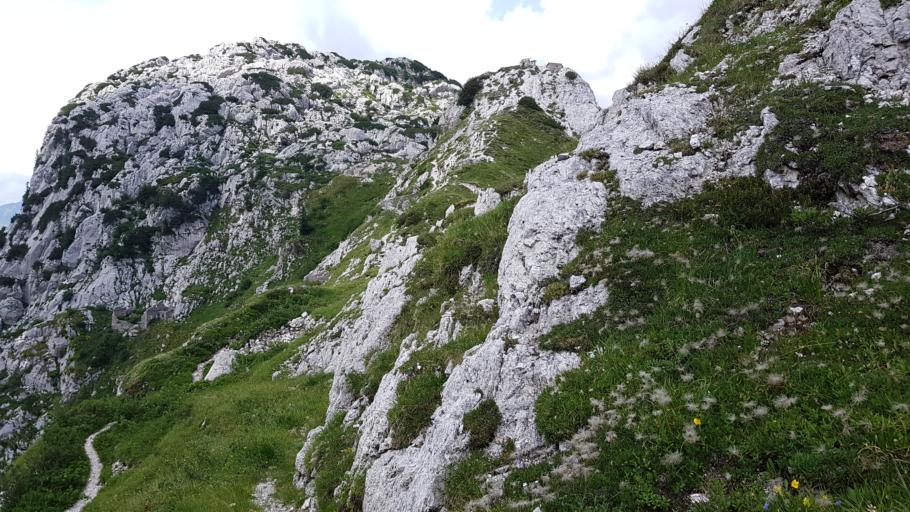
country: SI
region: Bovec
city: Bovec
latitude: 46.3829
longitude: 13.5169
